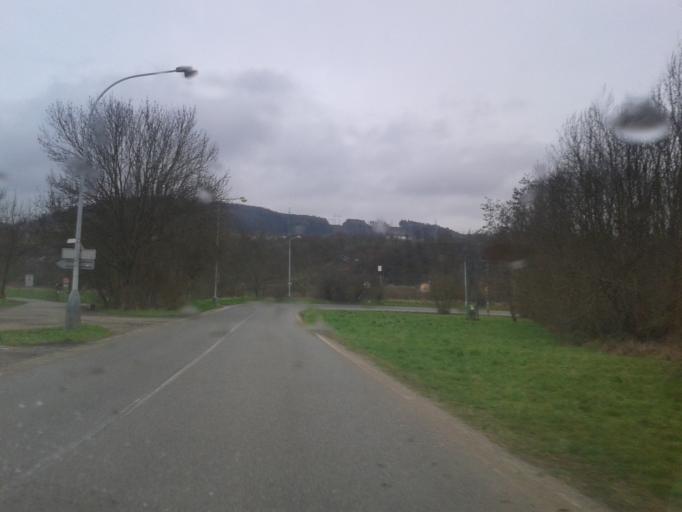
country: CZ
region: Central Bohemia
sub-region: Okres Beroun
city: Beroun
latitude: 49.9618
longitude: 14.0886
